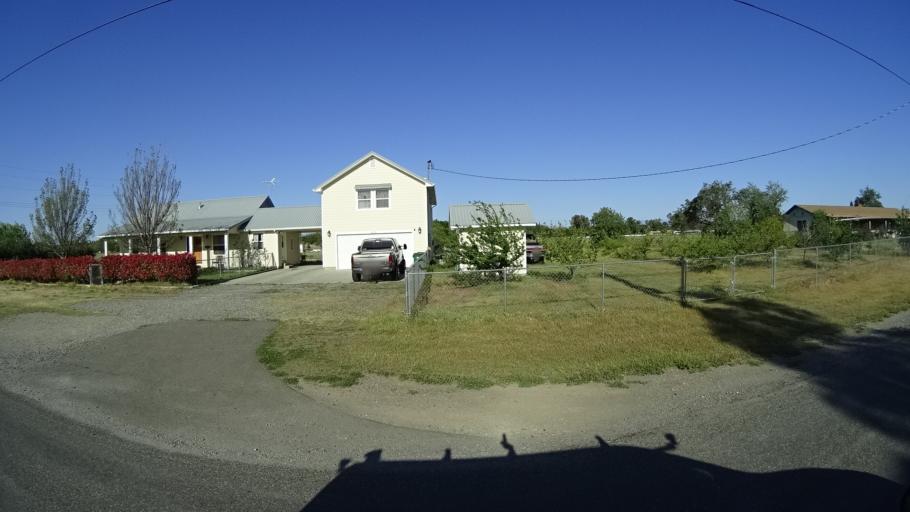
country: US
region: California
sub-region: Glenn County
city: Orland
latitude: 39.7261
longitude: -122.1877
